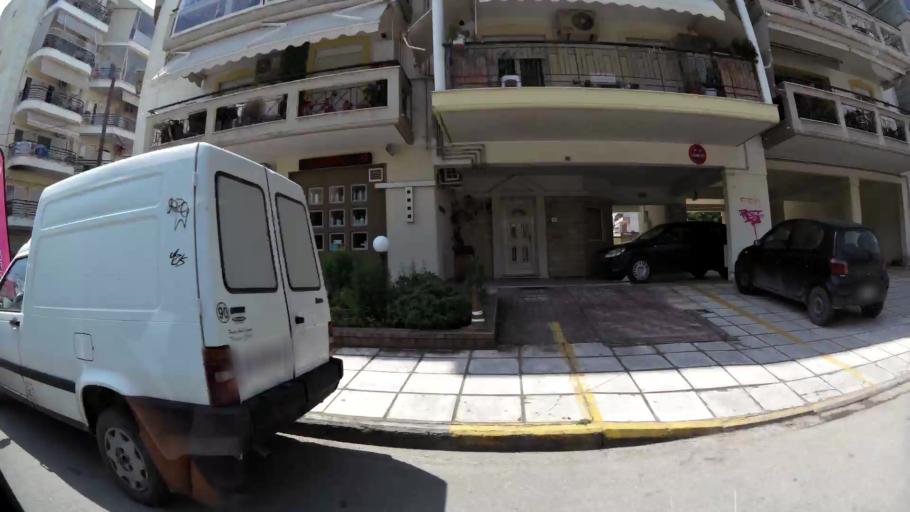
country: GR
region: Central Macedonia
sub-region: Nomos Thessalonikis
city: Evosmos
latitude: 40.6730
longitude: 22.9119
